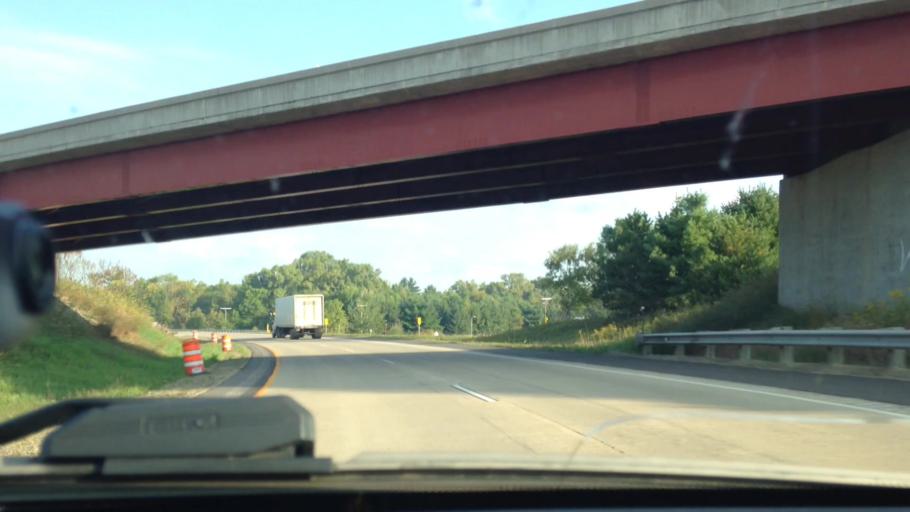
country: US
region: Wisconsin
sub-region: Oconto County
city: Oconto Falls
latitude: 44.7896
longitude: -88.0449
